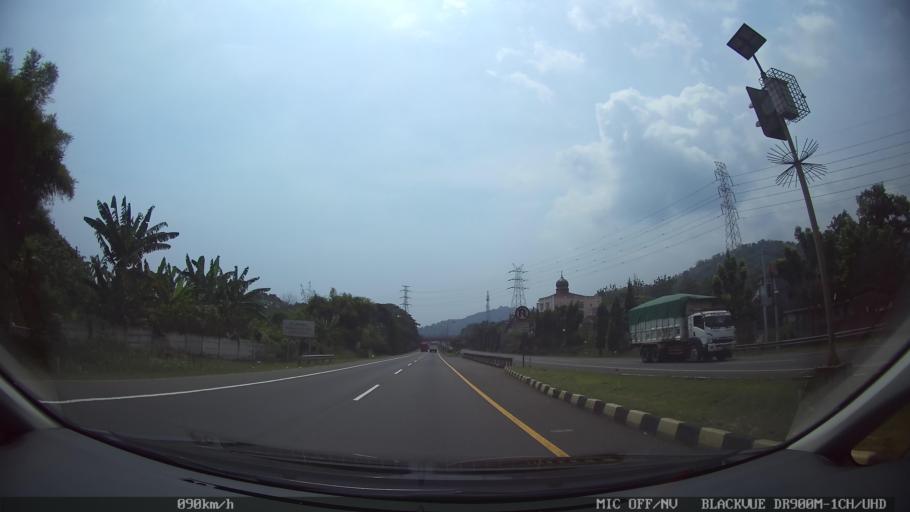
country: ID
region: Banten
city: Curug
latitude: -5.9894
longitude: 106.0399
